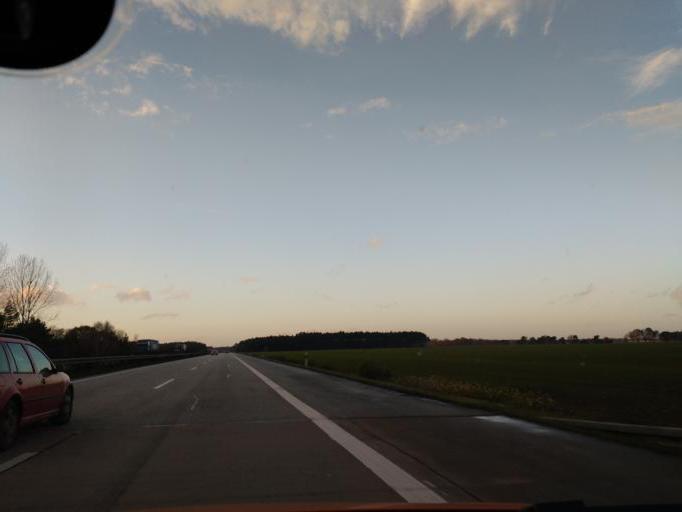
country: DE
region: Mecklenburg-Vorpommern
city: Sulstorf
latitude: 53.4486
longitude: 11.3667
